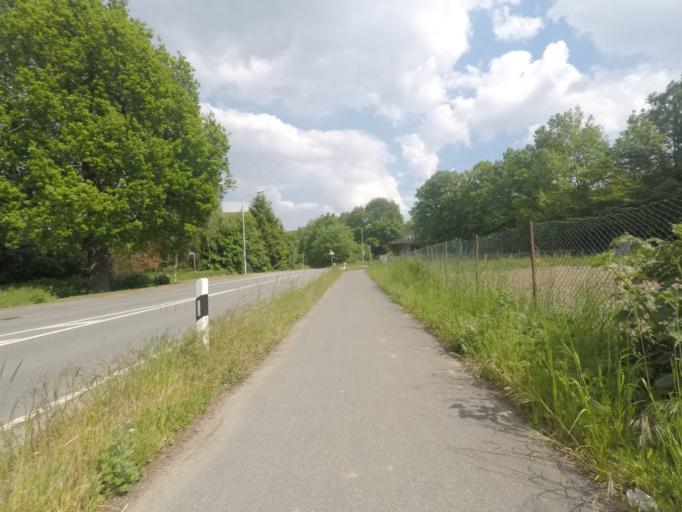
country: DE
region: North Rhine-Westphalia
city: Buende
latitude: 52.1939
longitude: 8.5252
